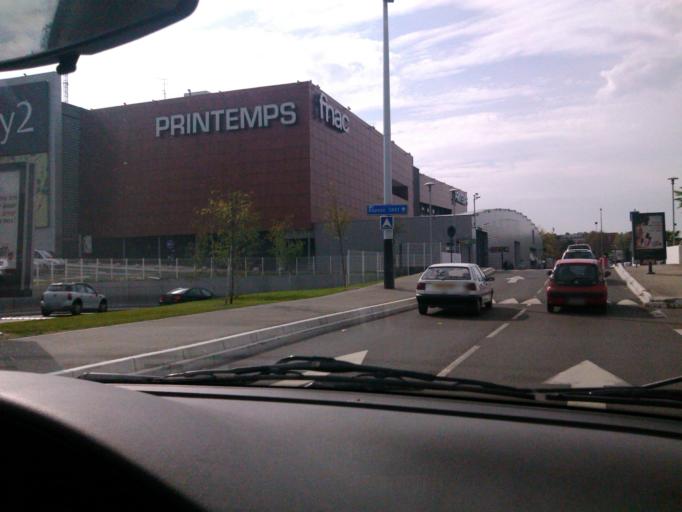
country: FR
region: Ile-de-France
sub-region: Departement des Hauts-de-Seine
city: Sevres
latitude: 48.8272
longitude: 2.2242
